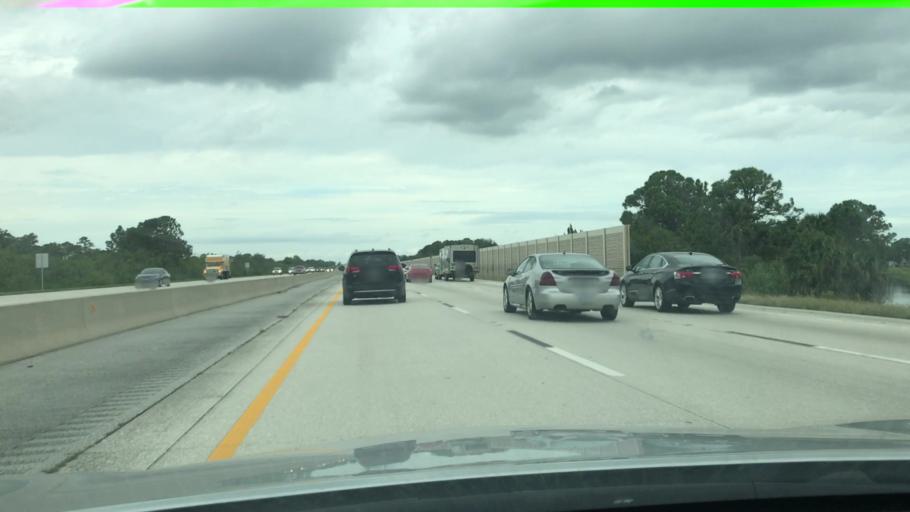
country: US
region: Florida
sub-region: Brevard County
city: Cocoa West
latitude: 28.3501
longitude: -80.7882
